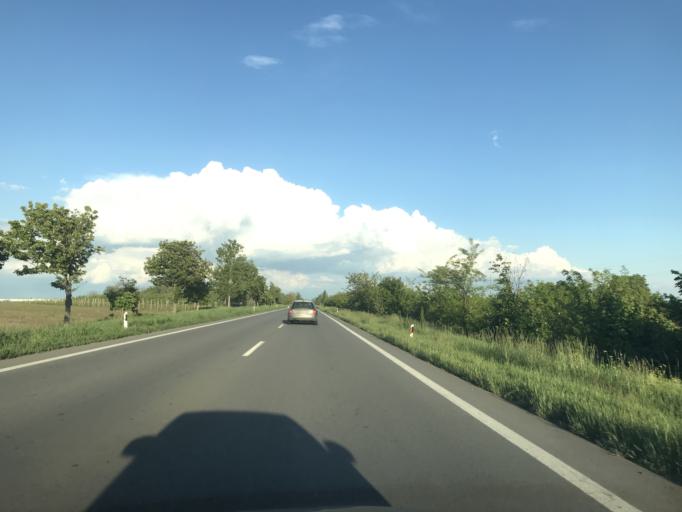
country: RS
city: Aradac
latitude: 45.3866
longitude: 20.3174
